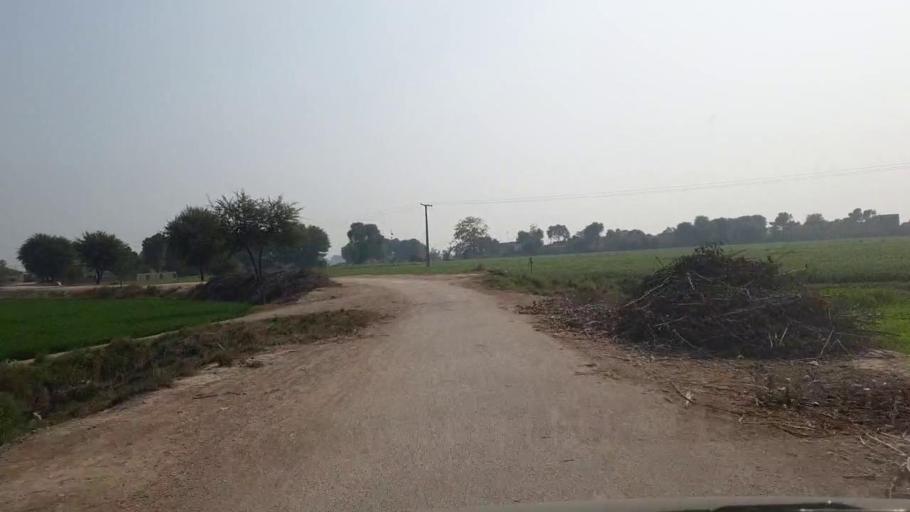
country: PK
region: Sindh
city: Bhit Shah
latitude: 25.8452
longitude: 68.4933
